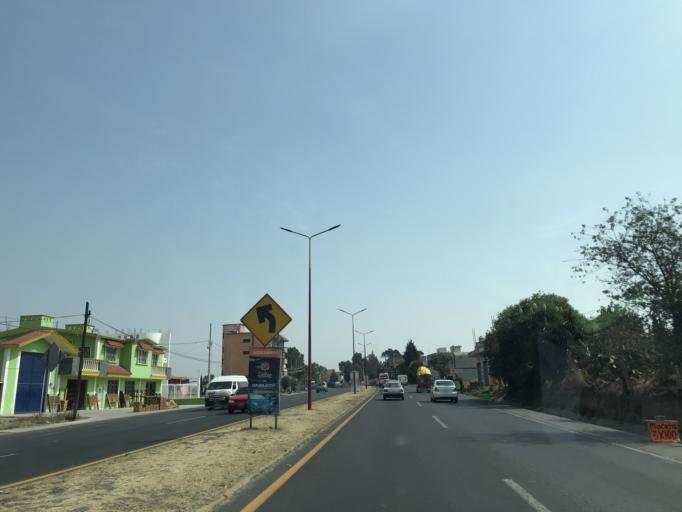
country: MX
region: Tlaxcala
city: La Magdalena Tlaltelulco
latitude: 19.2732
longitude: -98.1972
